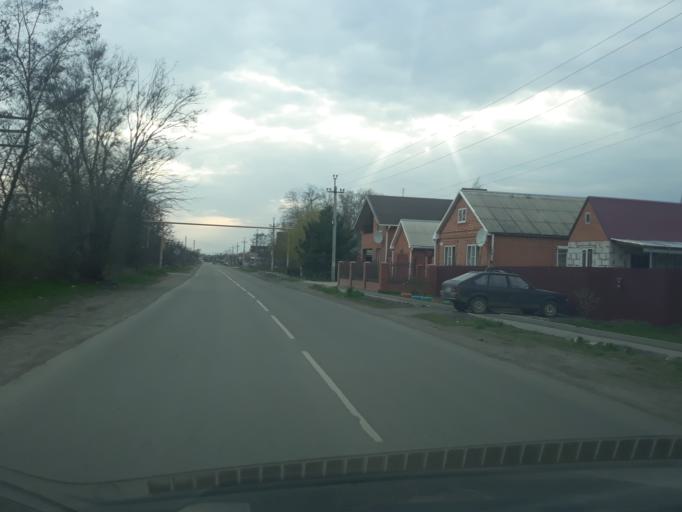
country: RU
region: Rostov
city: Novobessergenovka
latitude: 47.1759
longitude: 38.7716
